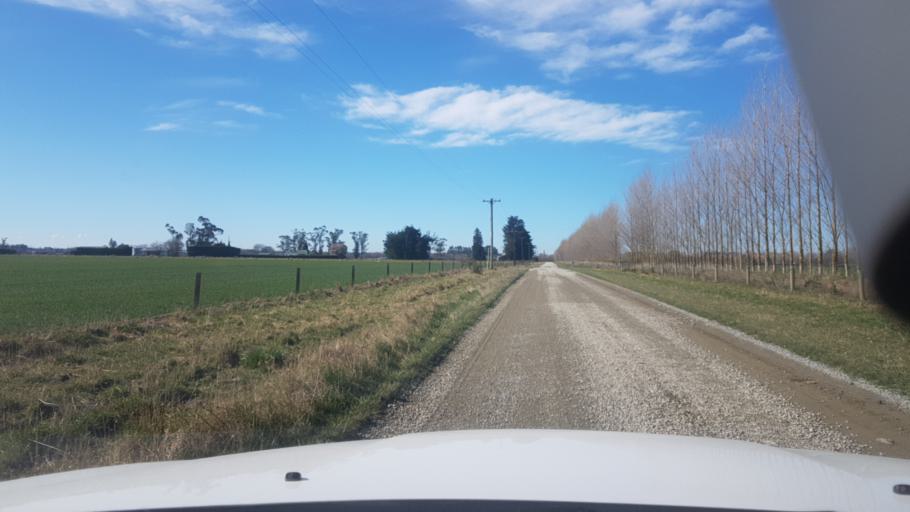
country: NZ
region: Canterbury
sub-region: Timaru District
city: Pleasant Point
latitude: -44.1447
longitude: 171.2387
